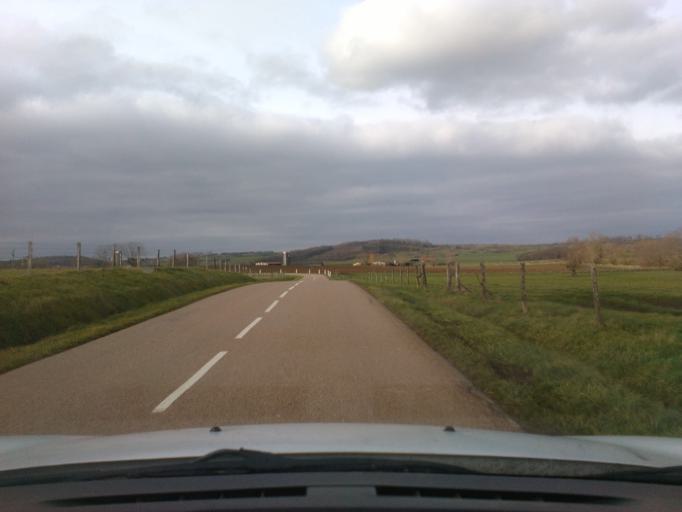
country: FR
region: Lorraine
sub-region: Departement des Vosges
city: Mirecourt
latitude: 48.3310
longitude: 6.0318
